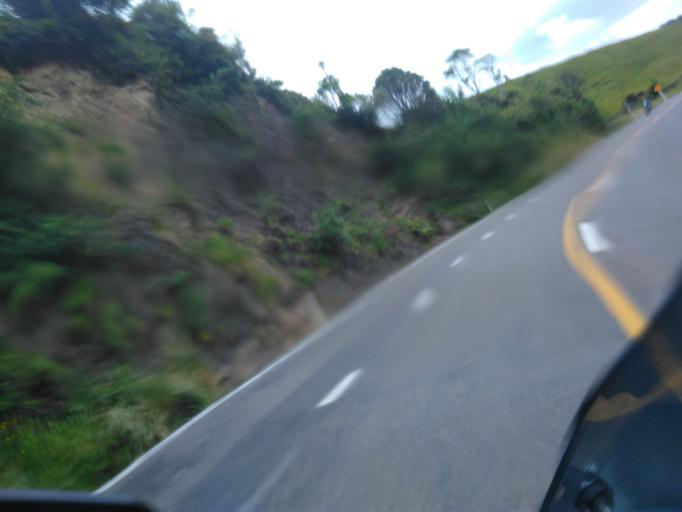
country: NZ
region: Bay of Plenty
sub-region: Opotiki District
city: Opotiki
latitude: -38.3523
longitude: 177.4507
